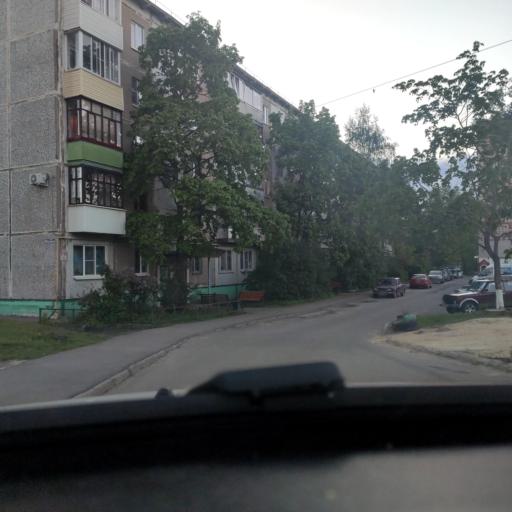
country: RU
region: Voronezj
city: Novovoronezh
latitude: 51.3165
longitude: 39.2069
